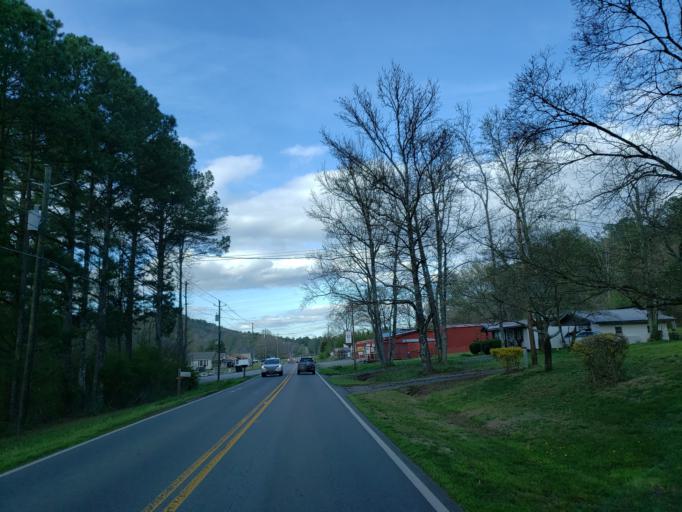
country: US
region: Georgia
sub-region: Bartow County
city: Cartersville
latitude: 34.2336
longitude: -84.8179
